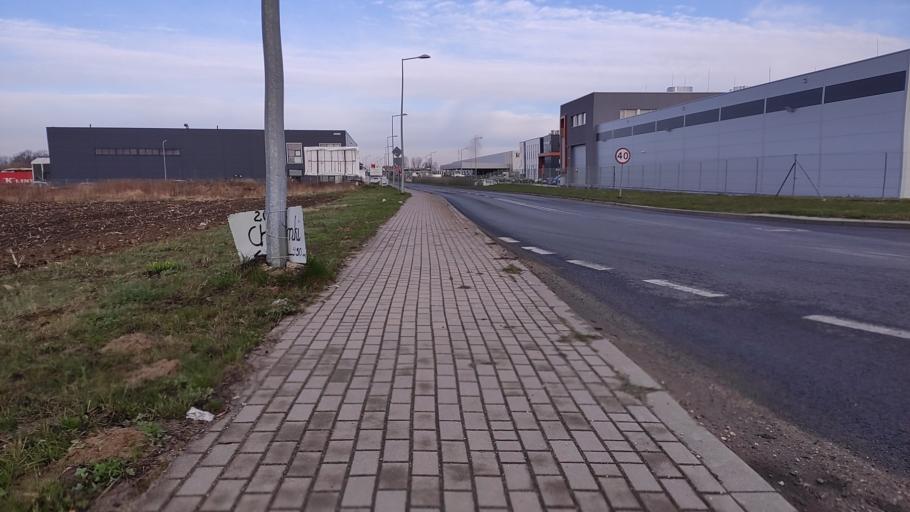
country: PL
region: Greater Poland Voivodeship
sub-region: Powiat poznanski
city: Swarzedz
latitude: 52.3973
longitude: 17.1209
